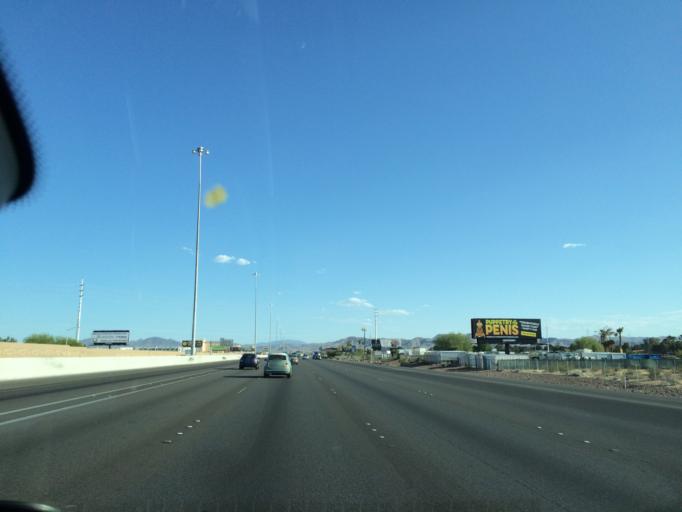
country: US
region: Nevada
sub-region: Clark County
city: Enterprise
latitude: 36.0375
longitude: -115.1809
